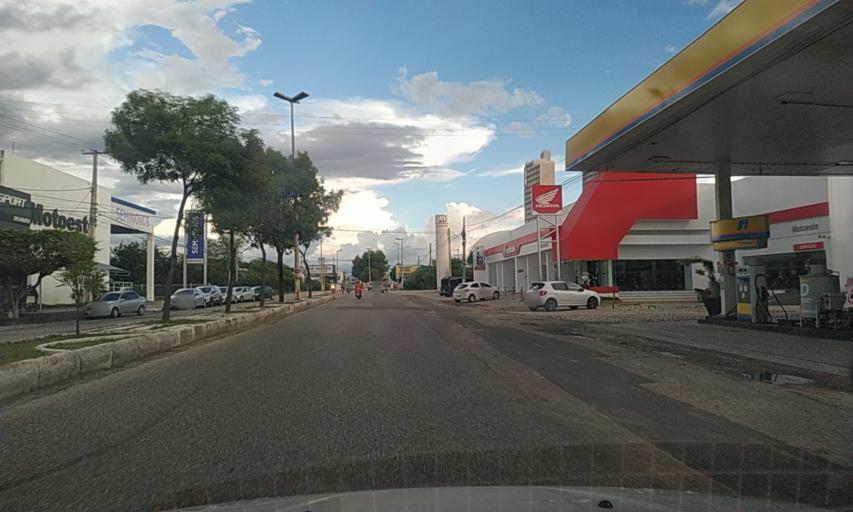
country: BR
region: Rio Grande do Norte
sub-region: Mossoro
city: Mossoro
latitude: -5.1992
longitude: -37.3399
